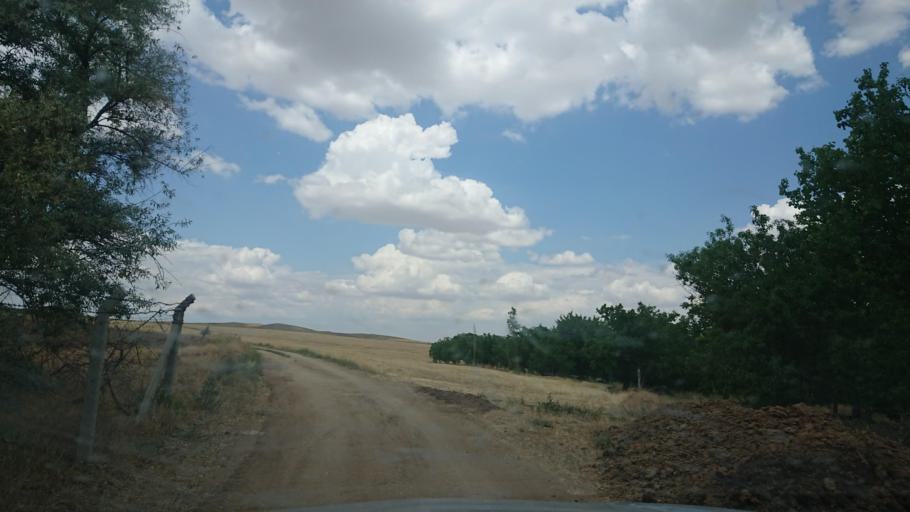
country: TR
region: Aksaray
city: Agacoren
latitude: 38.8926
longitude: 33.8829
